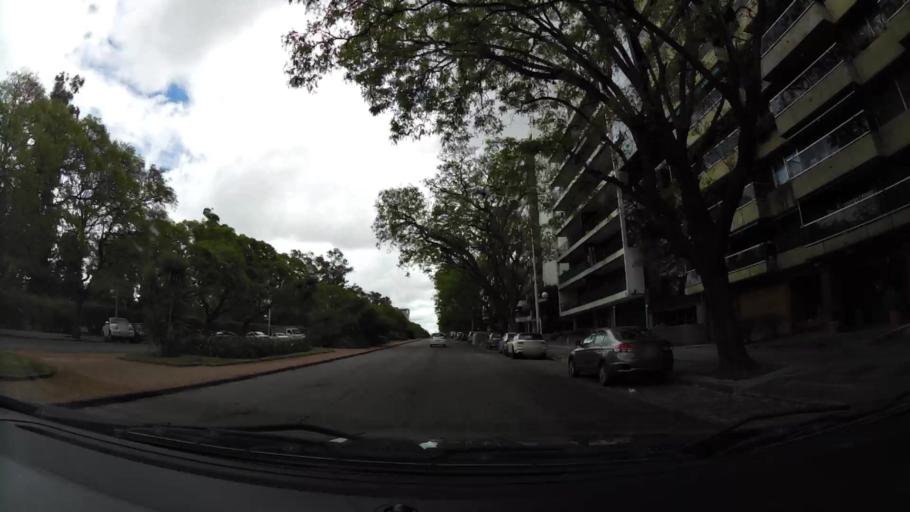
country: UY
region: Montevideo
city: Montevideo
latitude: -34.9250
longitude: -56.1616
